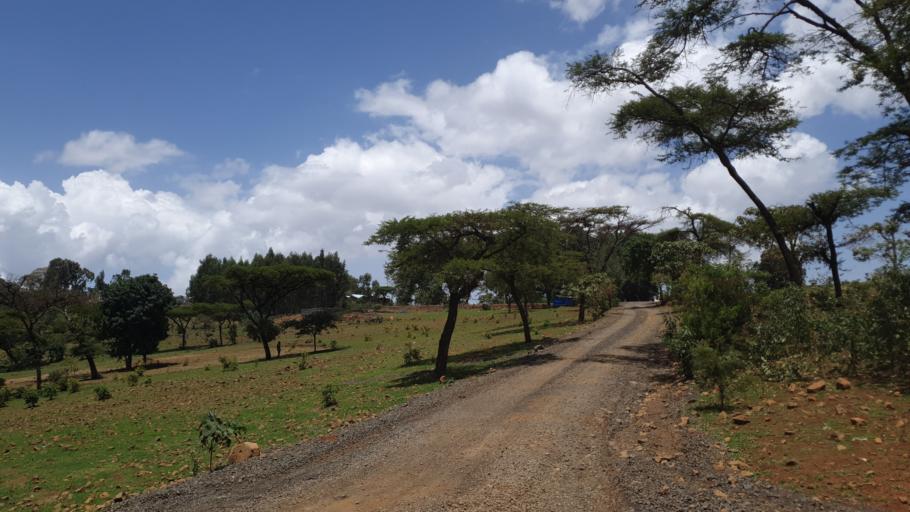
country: ET
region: Oromiya
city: Shambu
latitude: 10.0227
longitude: 36.8834
